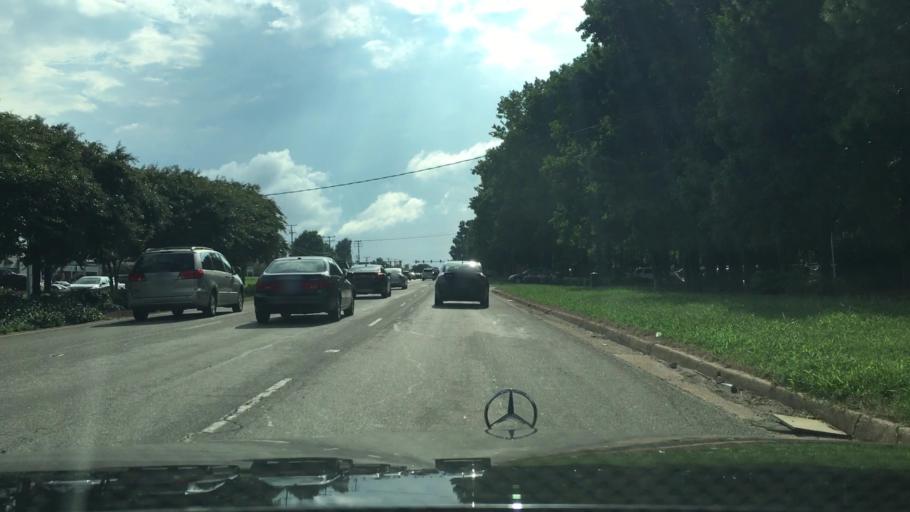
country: US
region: Virginia
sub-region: Chesterfield County
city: Bon Air
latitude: 37.5071
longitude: -77.5942
